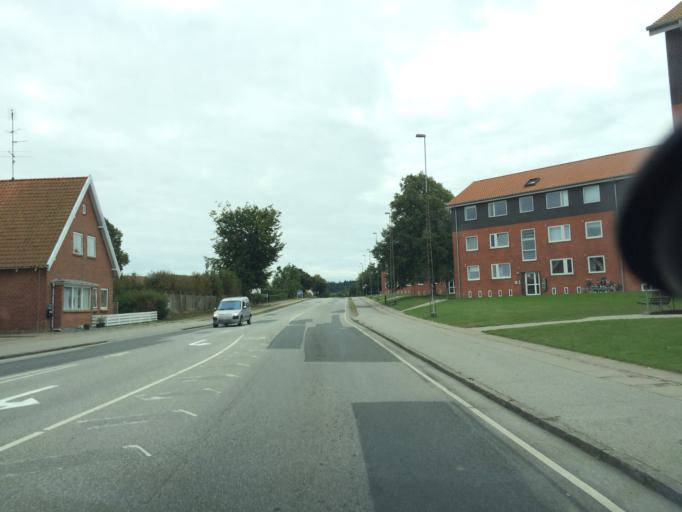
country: DK
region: South Denmark
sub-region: Aabenraa Kommune
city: Aabenraa
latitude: 55.0338
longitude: 9.4079
